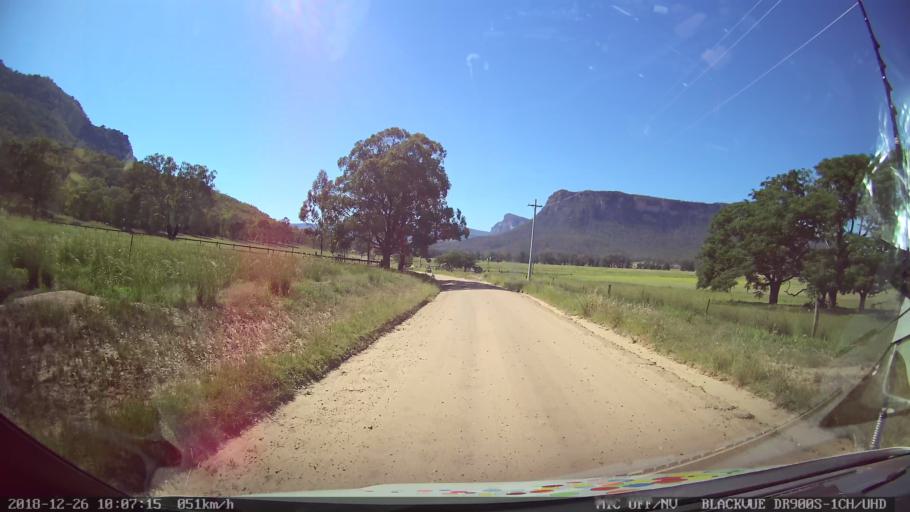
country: AU
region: New South Wales
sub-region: Mid-Western Regional
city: Kandos
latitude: -33.0897
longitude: 150.2231
